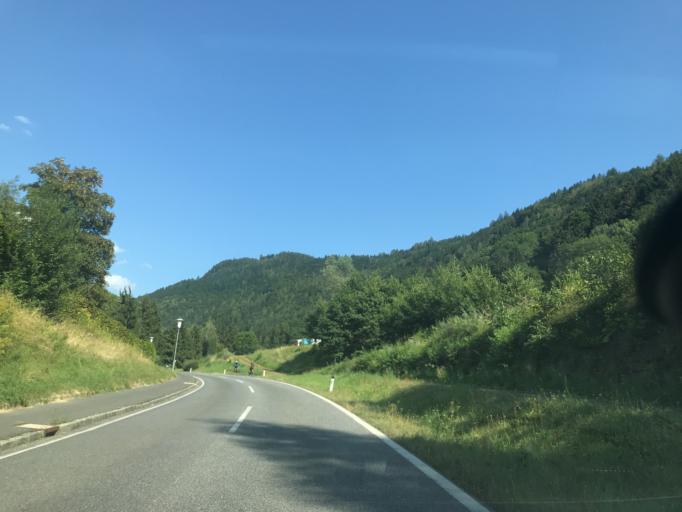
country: AT
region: Carinthia
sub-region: Politischer Bezirk Villach Land
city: Wernberg
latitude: 46.6524
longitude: 13.9265
